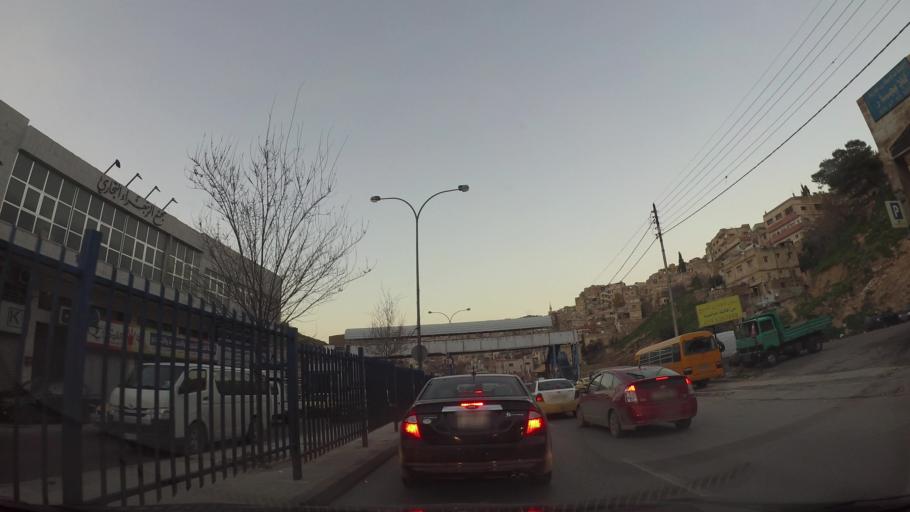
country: JO
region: Amman
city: Amman
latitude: 31.9363
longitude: 35.9233
